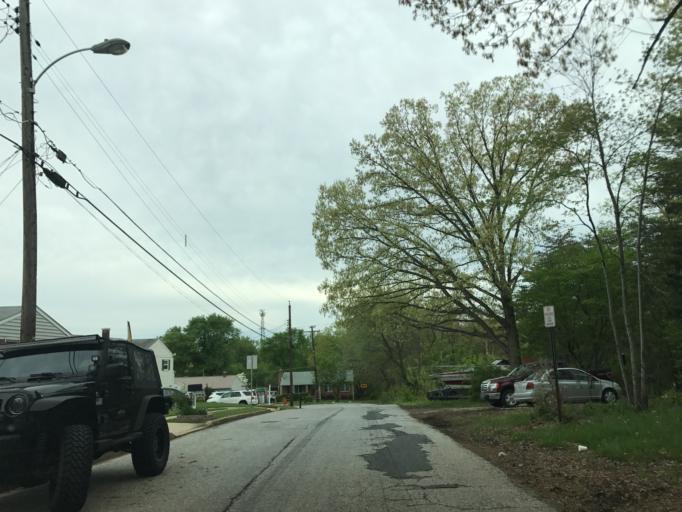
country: US
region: Maryland
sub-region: Baltimore County
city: Rosedale
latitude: 39.3147
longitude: -76.5127
